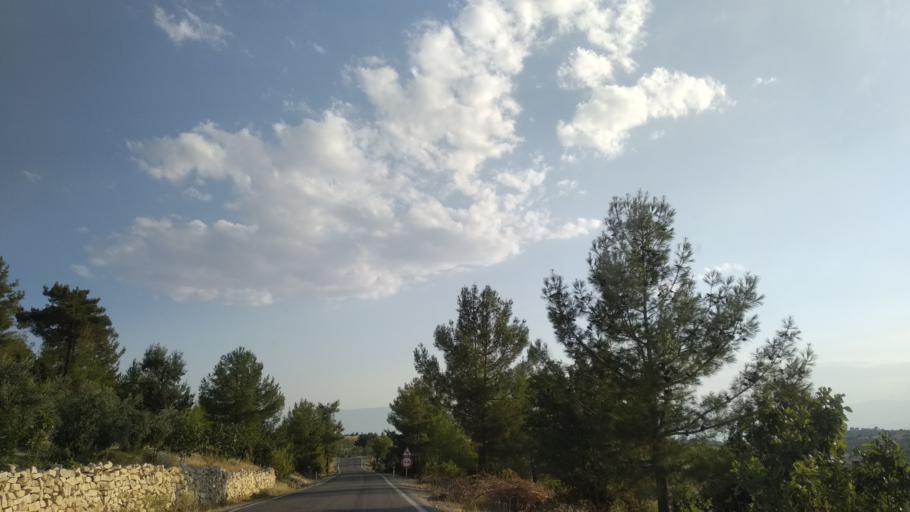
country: TR
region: Mersin
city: Sarikavak
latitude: 36.5749
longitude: 33.6392
